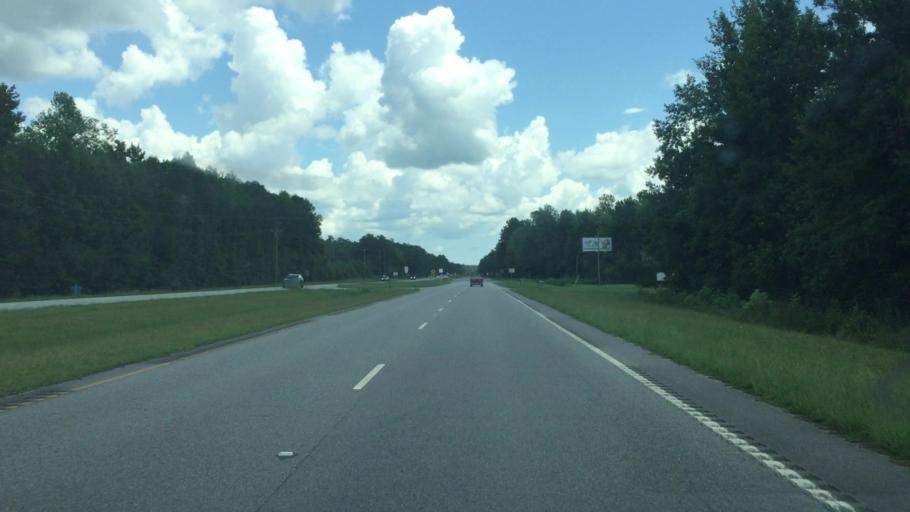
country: US
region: South Carolina
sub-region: Horry County
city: Loris
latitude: 34.0419
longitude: -78.8235
